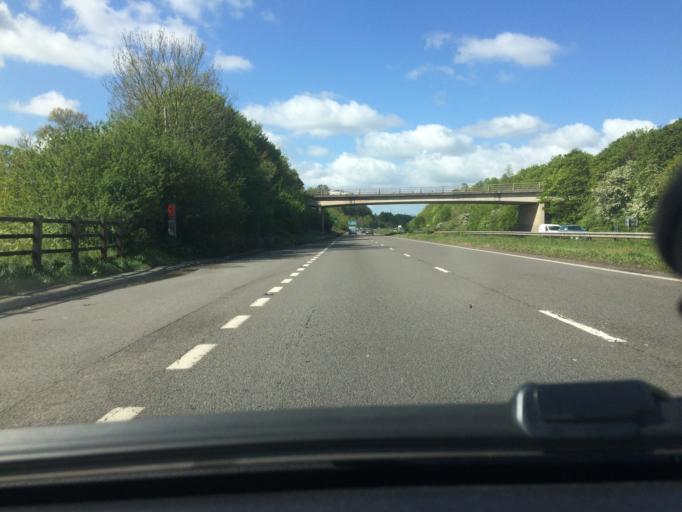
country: GB
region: England
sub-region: Cheshire West and Chester
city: Eccleston
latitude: 53.1622
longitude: -2.8796
